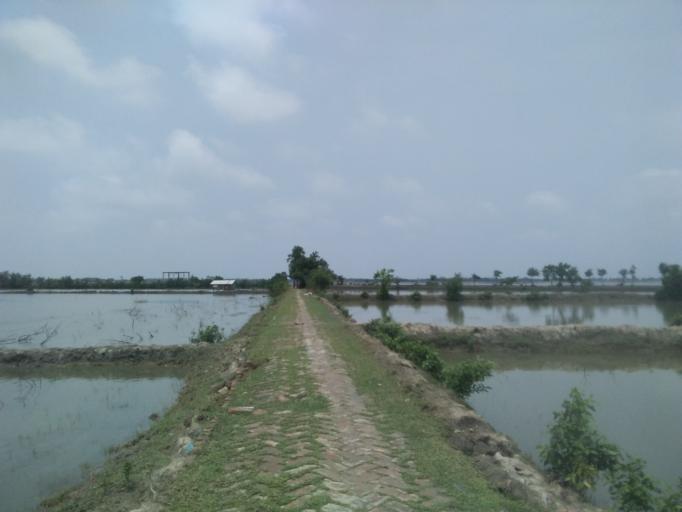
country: BD
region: Khulna
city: Phultala
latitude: 22.6417
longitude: 89.4156
